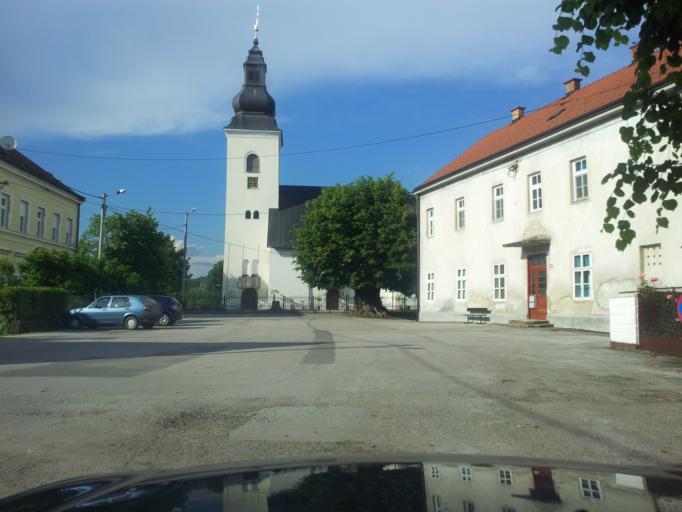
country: HR
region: Karlovacka
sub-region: Grad Karlovac
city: Karlovac
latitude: 45.4348
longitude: 15.4991
